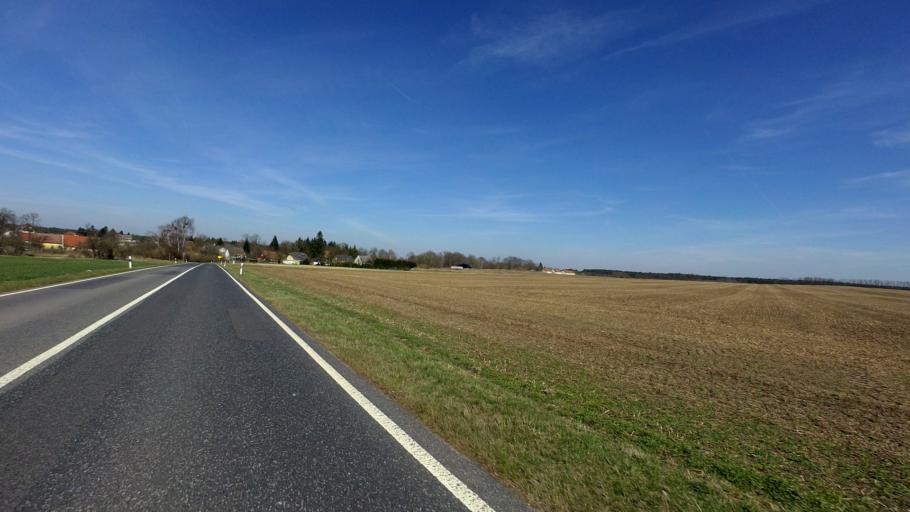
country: DE
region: Brandenburg
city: Waldsieversdorf
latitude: 52.4592
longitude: 14.0482
